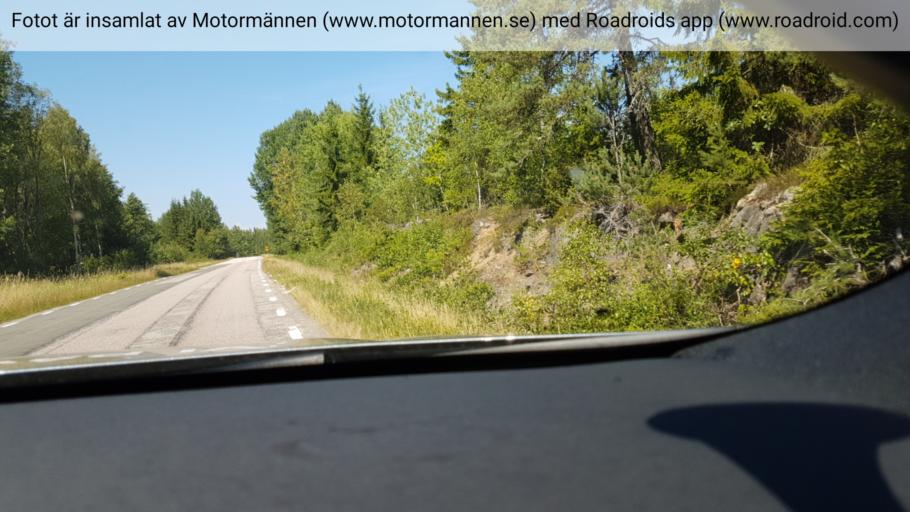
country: SE
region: Vaestra Goetaland
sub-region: Toreboda Kommun
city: Toereboda
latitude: 58.8292
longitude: 13.9955
